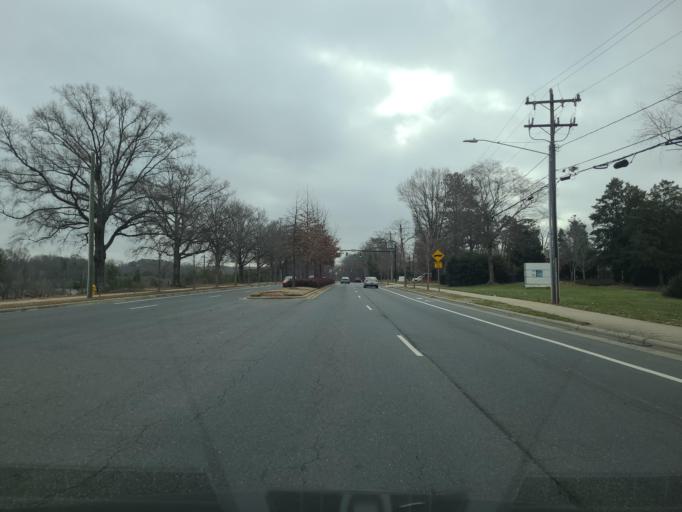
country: US
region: North Carolina
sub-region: Mecklenburg County
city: Charlotte
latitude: 35.2068
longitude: -80.7524
